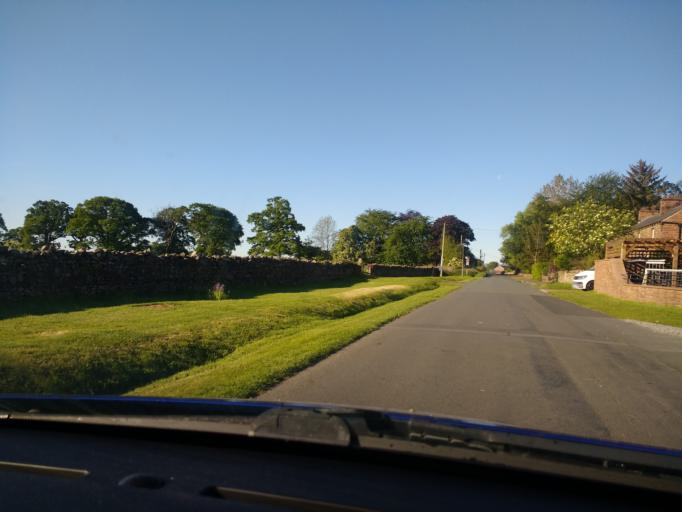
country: GB
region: England
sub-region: Cumbria
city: Appleby-in-Westmorland
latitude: 54.6613
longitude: -2.6046
